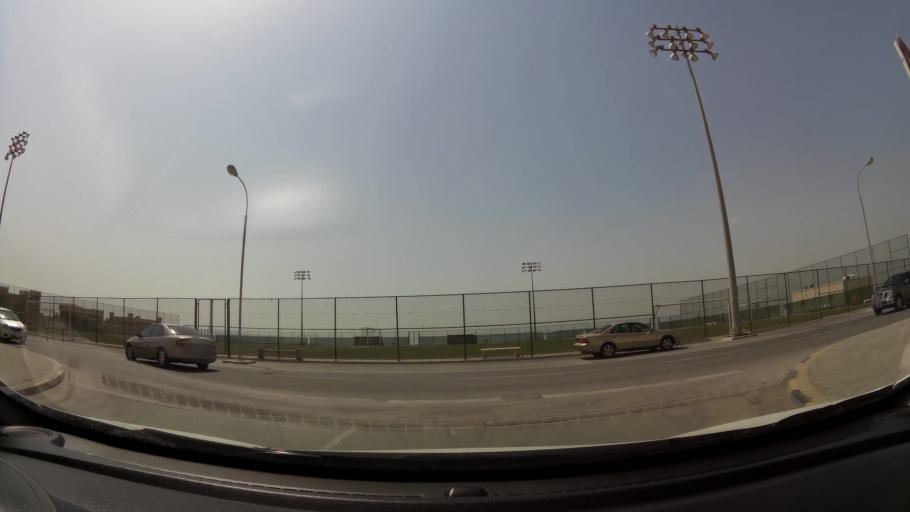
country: BH
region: Manama
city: Jidd Hafs
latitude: 26.2131
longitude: 50.4463
